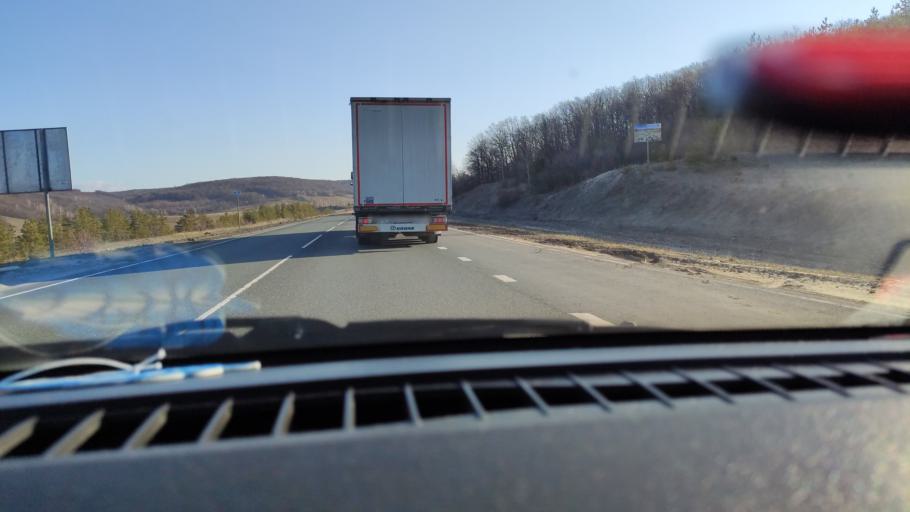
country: RU
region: Saratov
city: Alekseyevka
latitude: 52.3928
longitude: 47.9788
